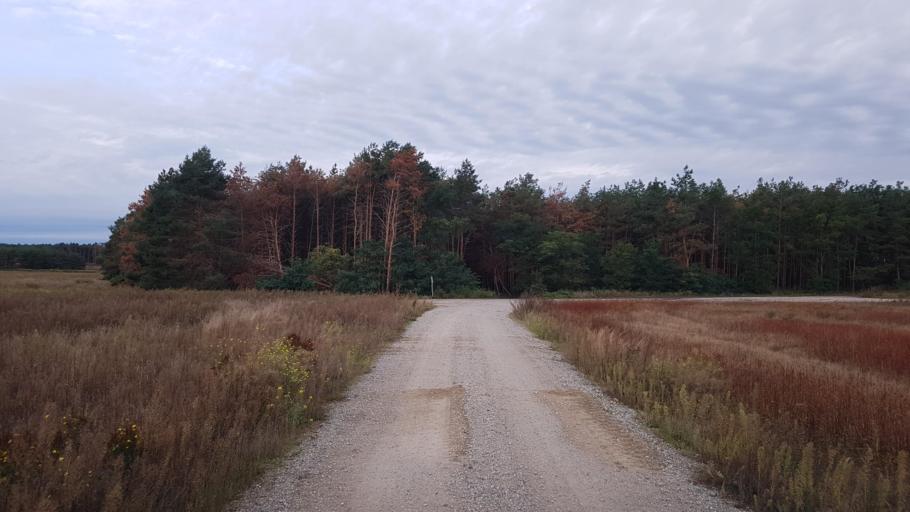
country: DE
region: Brandenburg
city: Kasel-Golzig
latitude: 51.9219
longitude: 13.7491
